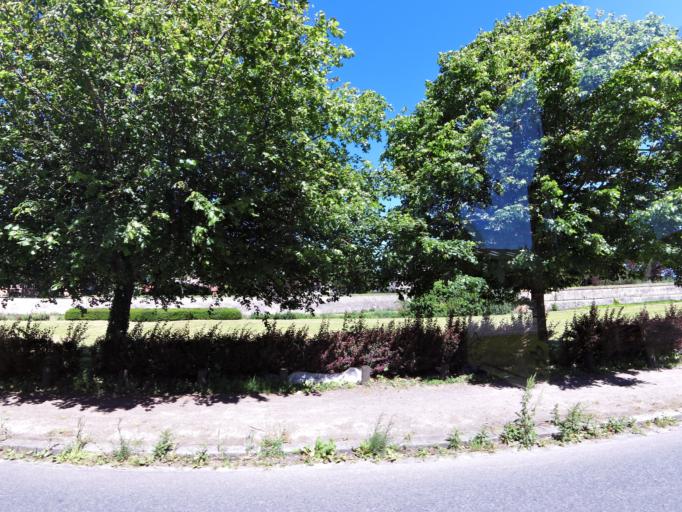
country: FR
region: Nord-Pas-de-Calais
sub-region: Departement du Nord
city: Bergues
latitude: 50.9652
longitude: 2.4310
